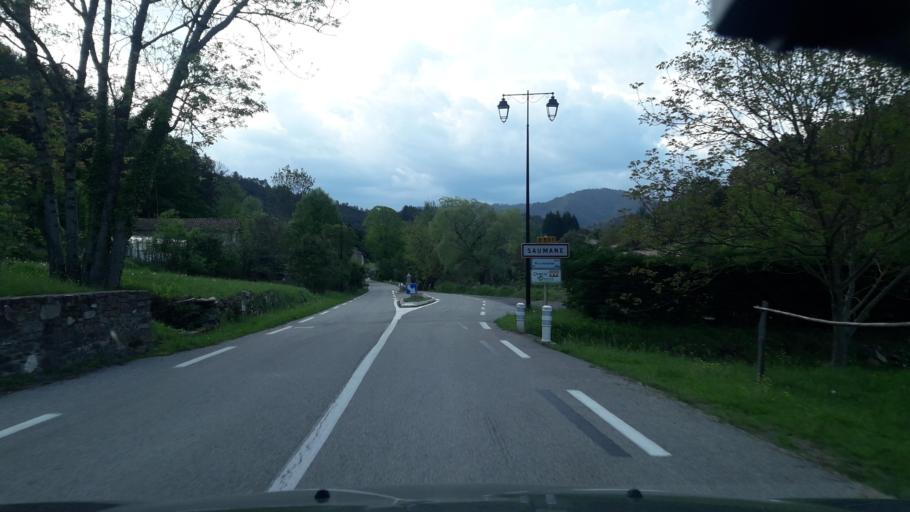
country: FR
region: Languedoc-Roussillon
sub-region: Departement du Gard
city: Lasalle
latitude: 44.1154
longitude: 3.7658
